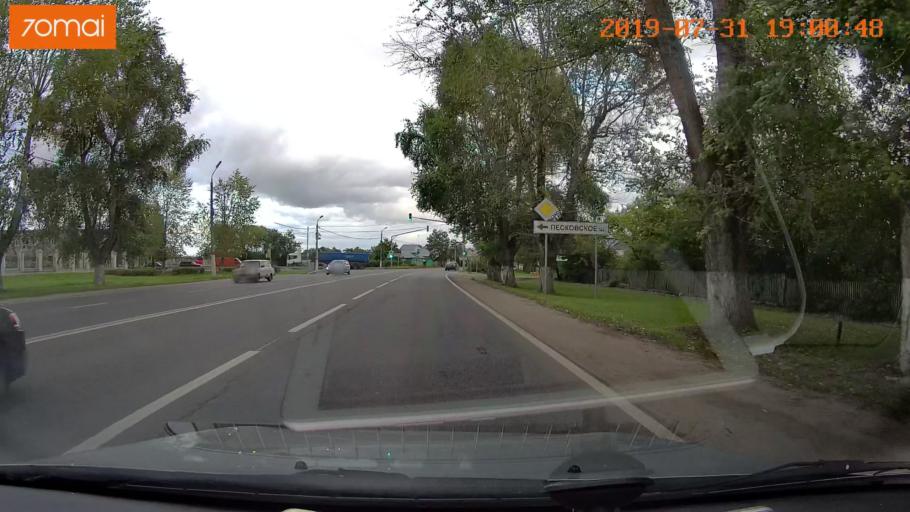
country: RU
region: Moskovskaya
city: Raduzhnyy
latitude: 55.1311
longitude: 38.7271
